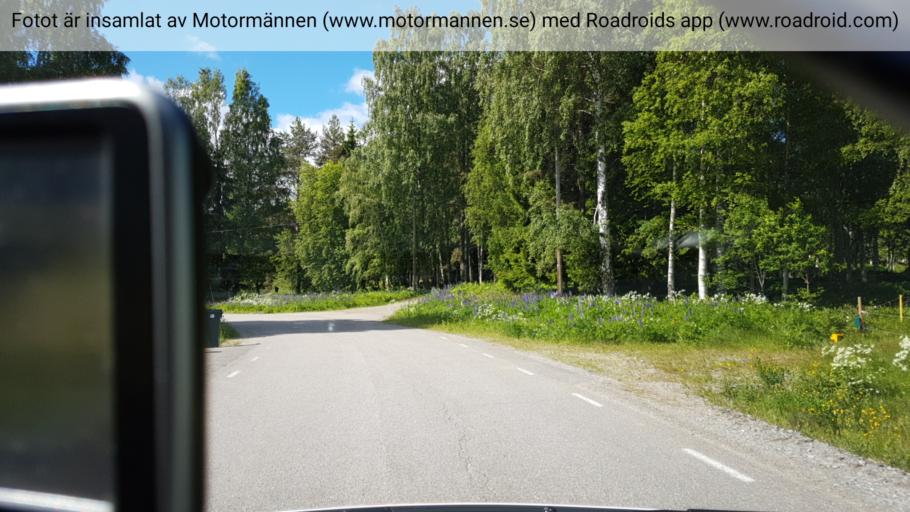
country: SE
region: Gaevleborg
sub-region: Hudiksvalls Kommun
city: Sorforsa
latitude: 61.6734
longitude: 16.9219
